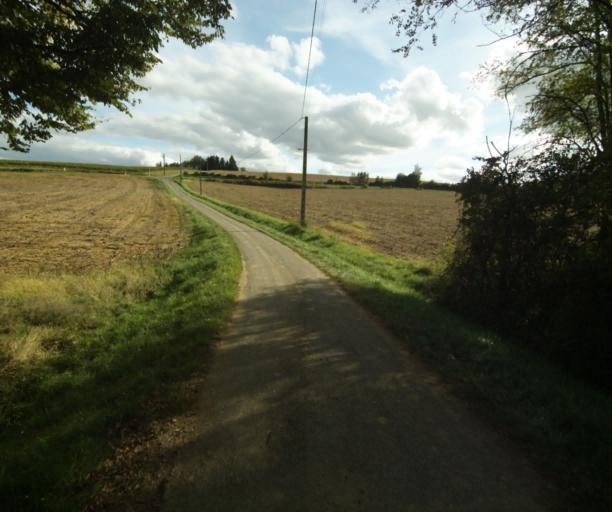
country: FR
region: Midi-Pyrenees
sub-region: Departement du Gers
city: Gondrin
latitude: 43.8458
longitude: 0.2749
